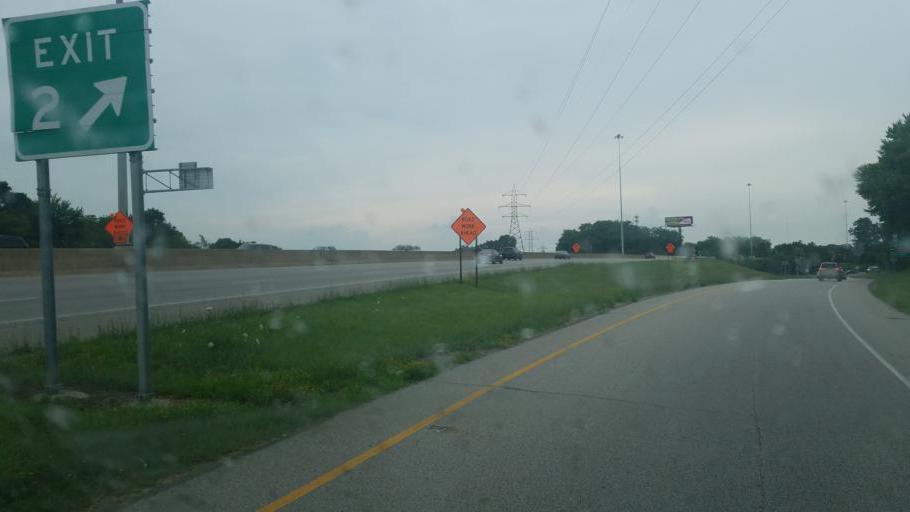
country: US
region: Ohio
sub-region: Summit County
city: Portage Lakes
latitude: 41.0279
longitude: -81.5444
